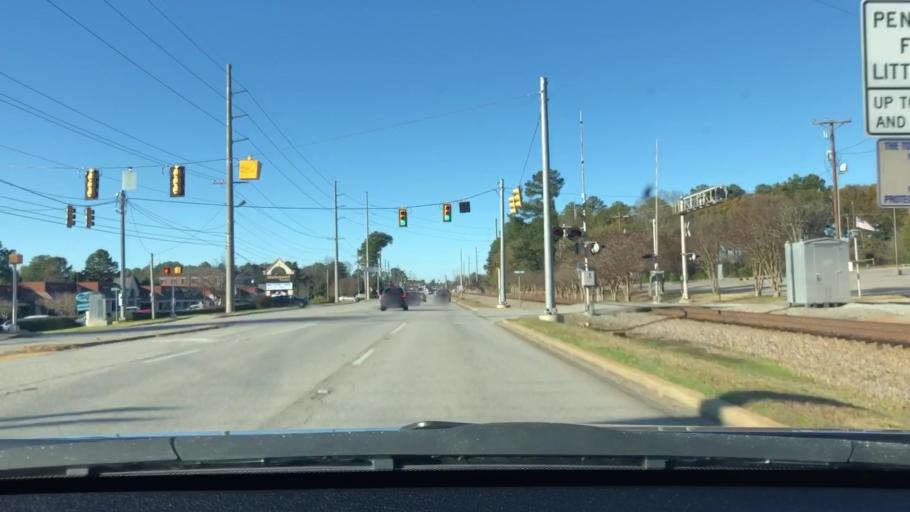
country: US
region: South Carolina
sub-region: Lexington County
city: Irmo
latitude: 34.0747
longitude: -81.1769
